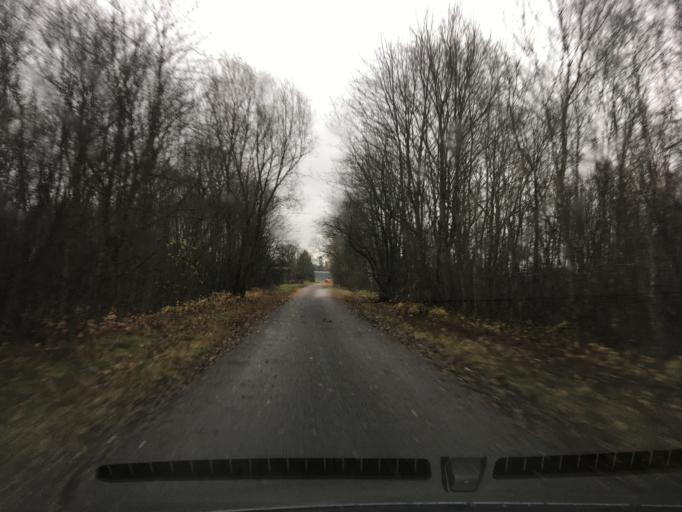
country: EE
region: Laeaene
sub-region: Lihula vald
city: Lihula
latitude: 58.5801
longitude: 23.7276
